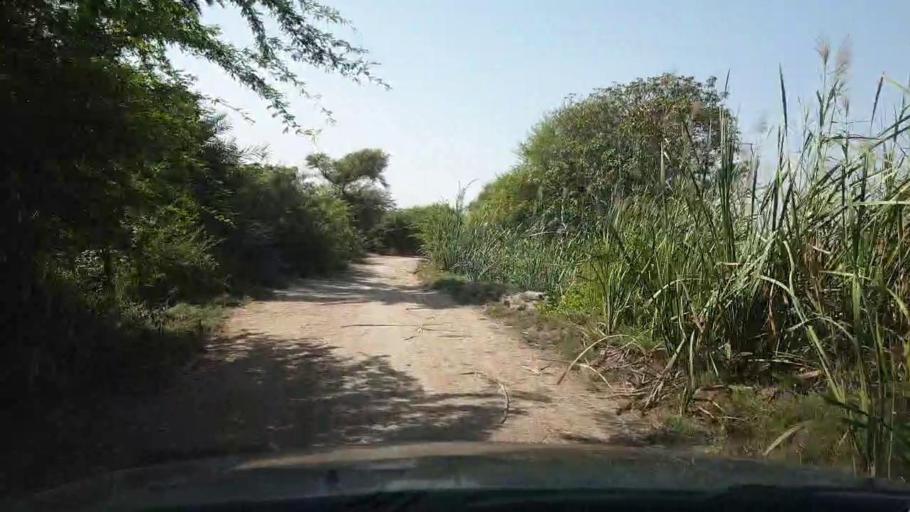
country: PK
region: Sindh
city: Daro Mehar
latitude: 24.9751
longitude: 68.1042
